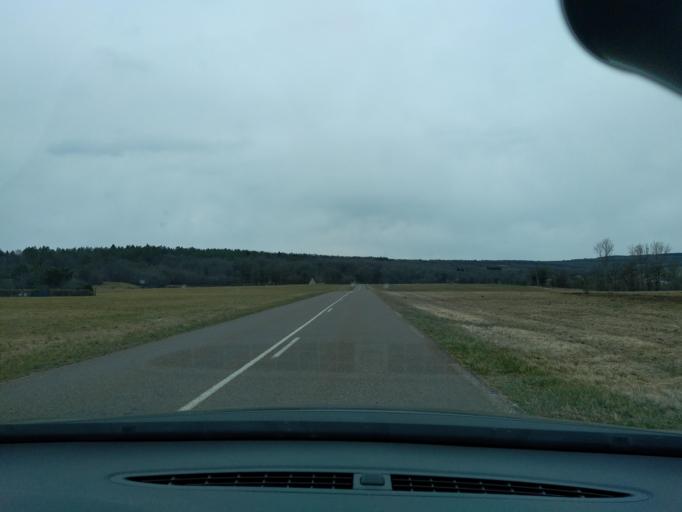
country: FR
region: Franche-Comte
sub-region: Departement du Jura
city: Arinthod
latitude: 46.4511
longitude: 5.5562
